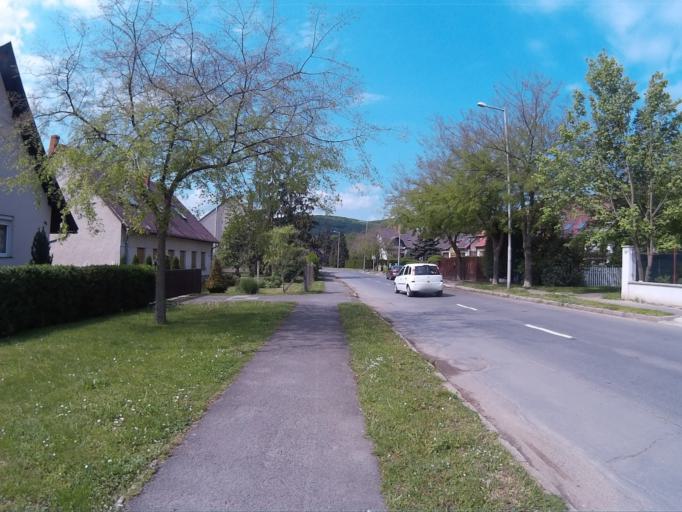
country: HU
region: Vas
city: Koszeg
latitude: 47.3847
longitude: 16.5347
